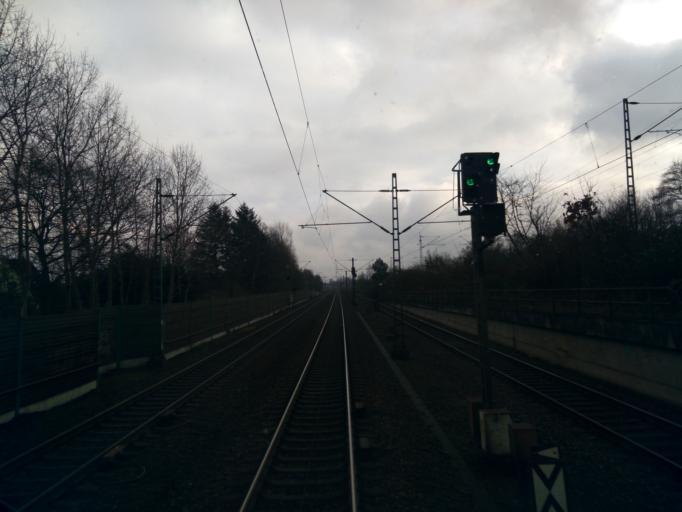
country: DE
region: Hamburg
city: Harburg
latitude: 53.4313
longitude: 10.0211
